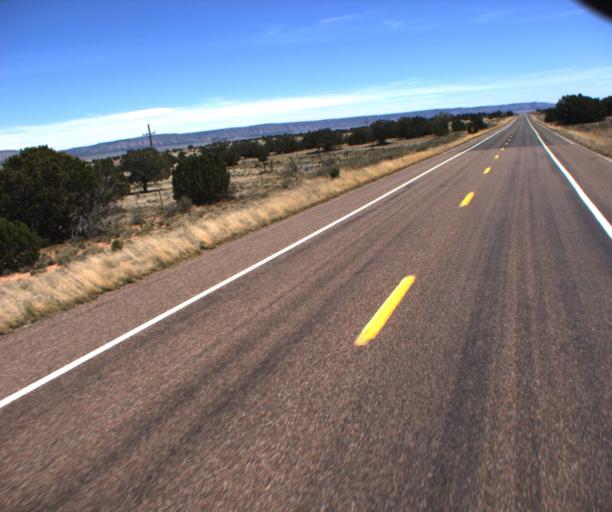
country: US
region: Arizona
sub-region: Mohave County
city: Peach Springs
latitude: 35.5079
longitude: -113.1842
